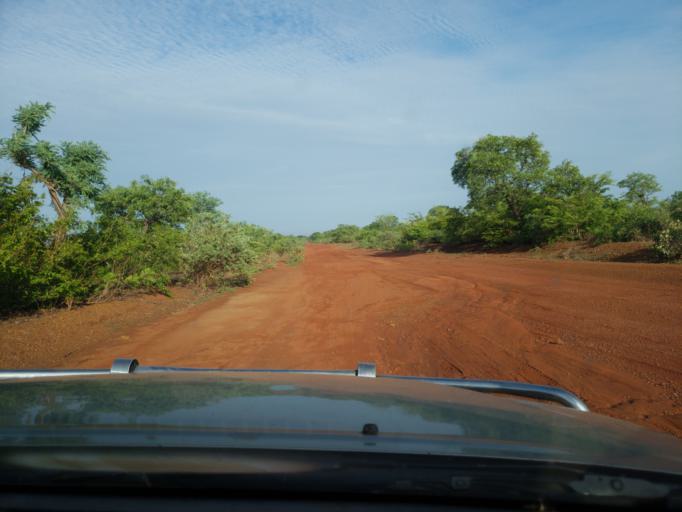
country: ML
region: Sikasso
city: Koutiala
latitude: 12.4258
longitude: -5.6473
